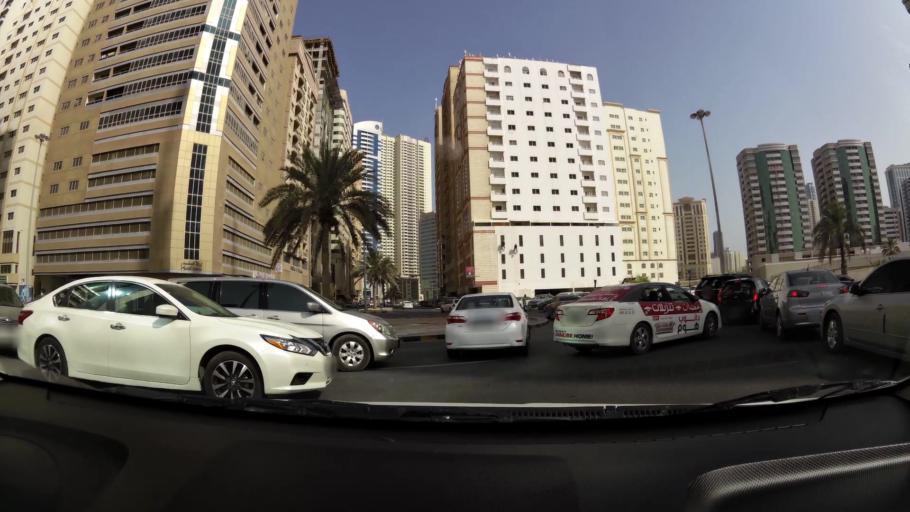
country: AE
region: Ash Shariqah
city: Sharjah
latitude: 25.3150
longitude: 55.3788
